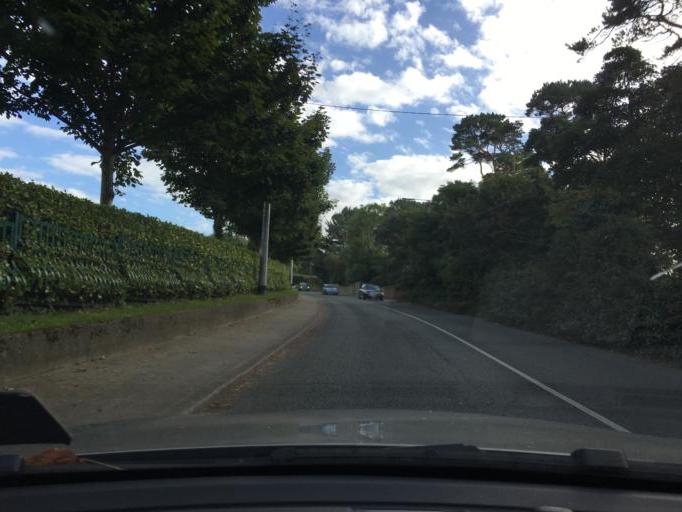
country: IE
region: Leinster
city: Sutton
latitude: 53.3747
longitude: -6.0899
